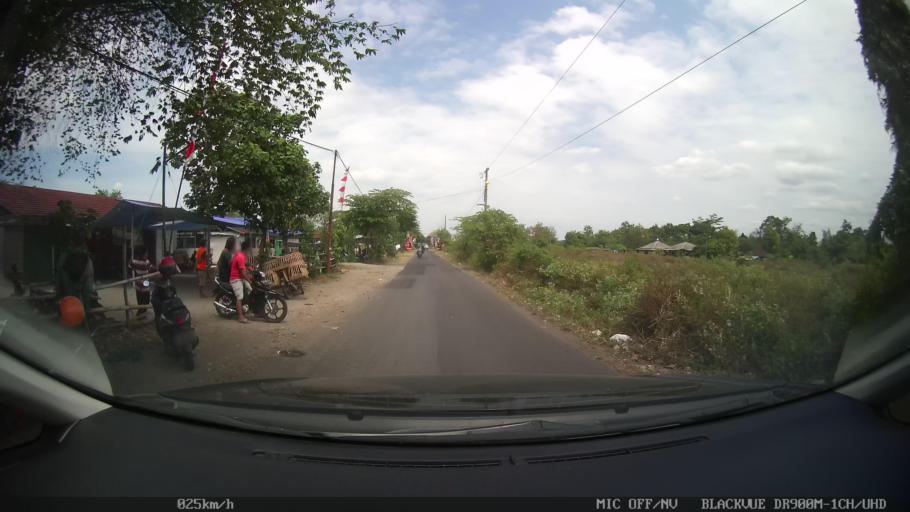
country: ID
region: Central Java
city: Candi Prambanan
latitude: -7.7731
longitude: 110.4790
